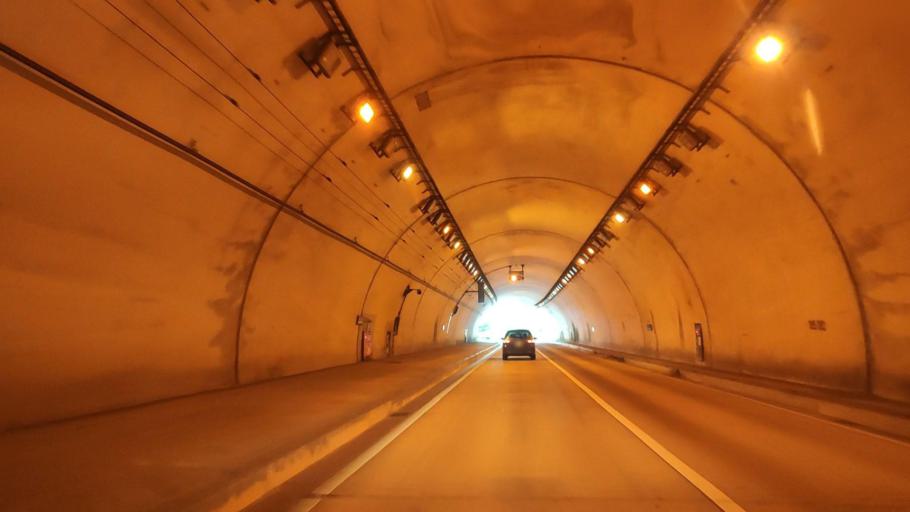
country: JP
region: Ehime
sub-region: Shikoku-chuo Shi
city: Matsuyama
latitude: 33.8867
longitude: 132.7073
